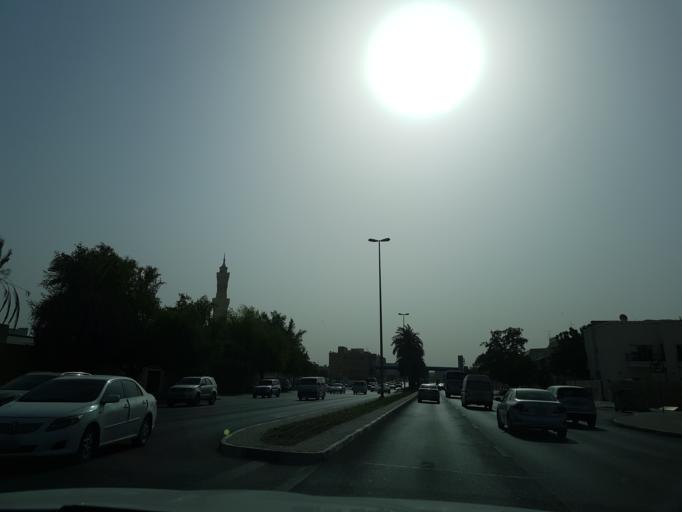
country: AE
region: Ash Shariqah
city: Sharjah
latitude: 25.2783
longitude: 55.3253
